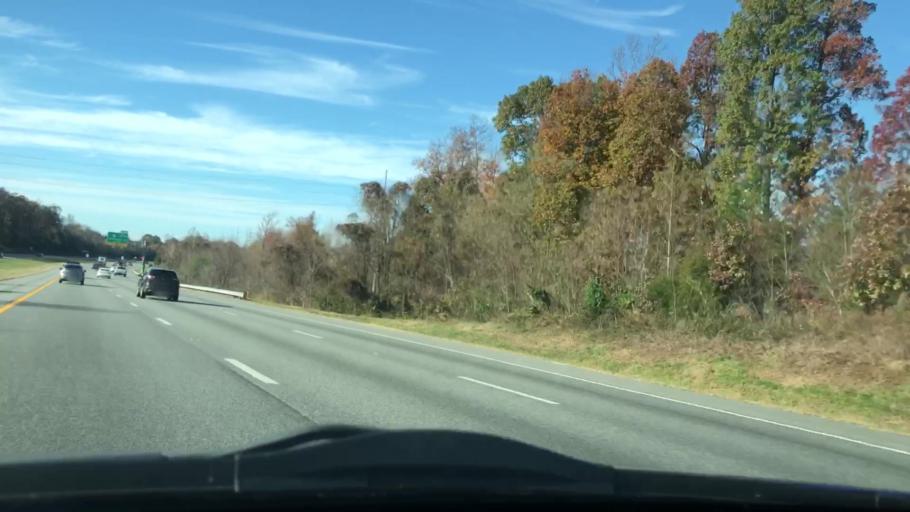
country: US
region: North Carolina
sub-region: Guilford County
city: High Point
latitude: 35.9900
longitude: -79.9813
